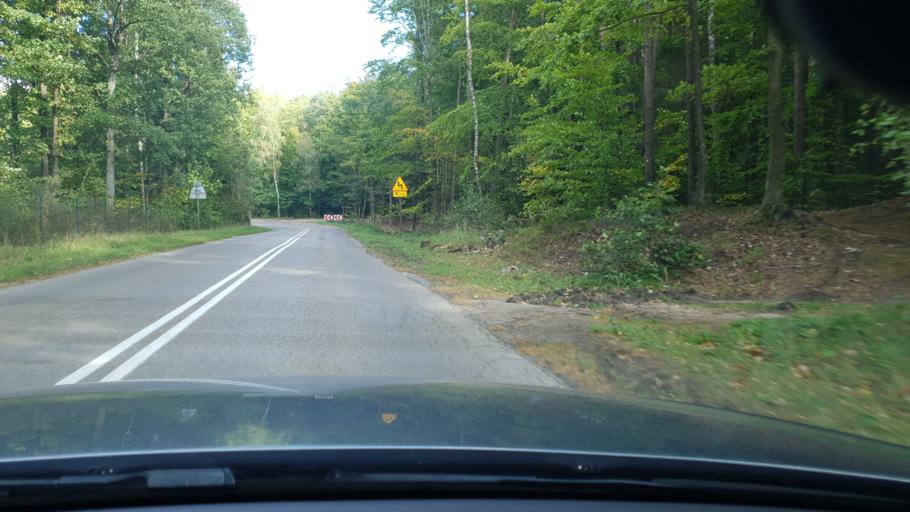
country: PL
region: Pomeranian Voivodeship
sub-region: Powiat wejherowski
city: Bojano
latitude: 54.5067
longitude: 18.3789
